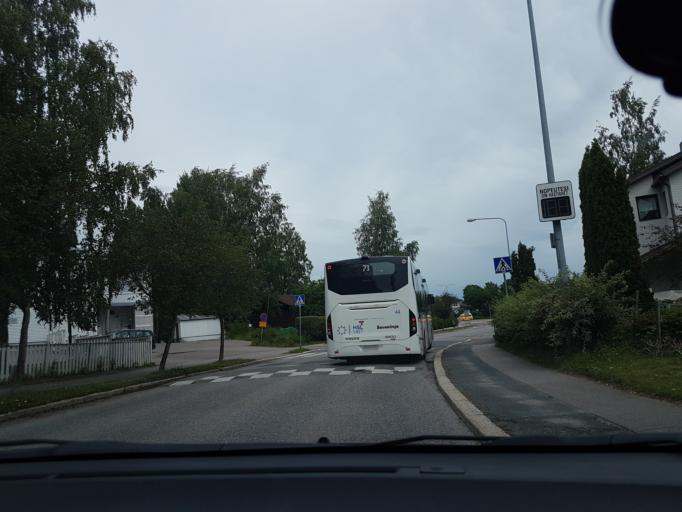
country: FI
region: Uusimaa
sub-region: Helsinki
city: Vantaa
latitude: 60.2598
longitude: 25.0019
